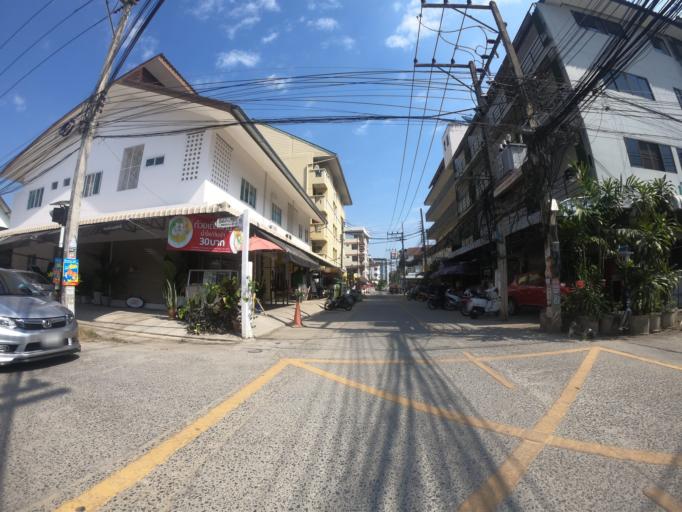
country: TH
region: Chiang Mai
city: Chiang Mai
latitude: 18.8064
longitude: 98.9902
